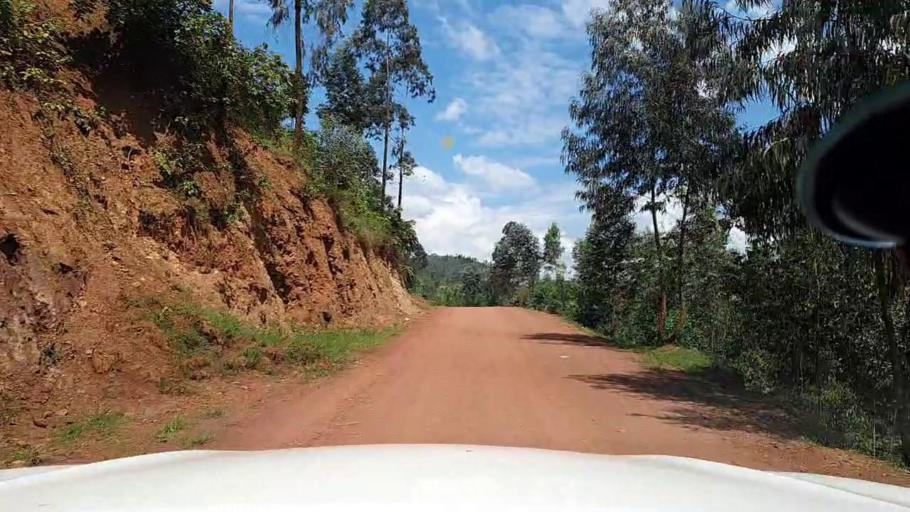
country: RW
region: Kigali
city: Kigali
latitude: -1.7774
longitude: 29.8753
